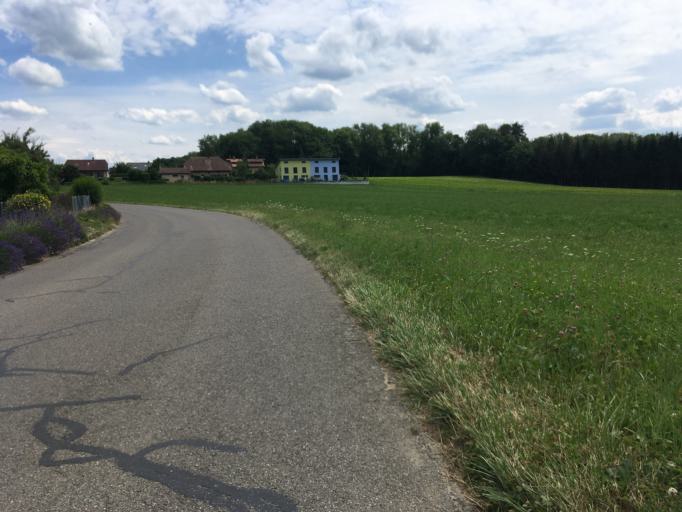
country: CH
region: Fribourg
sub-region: Broye District
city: Estavayer-le-Lac
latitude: 46.8698
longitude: 6.8808
